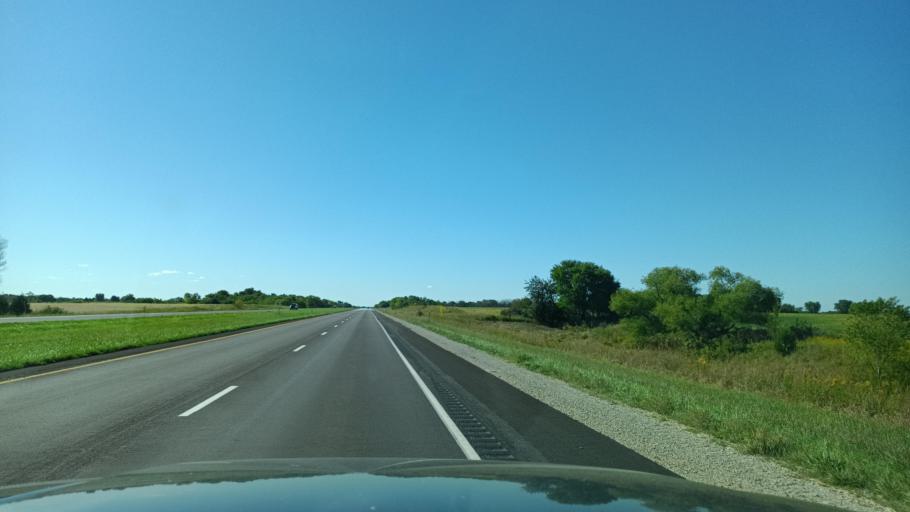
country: US
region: Illinois
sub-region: Hancock County
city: Nauvoo
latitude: 40.4887
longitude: -91.4438
